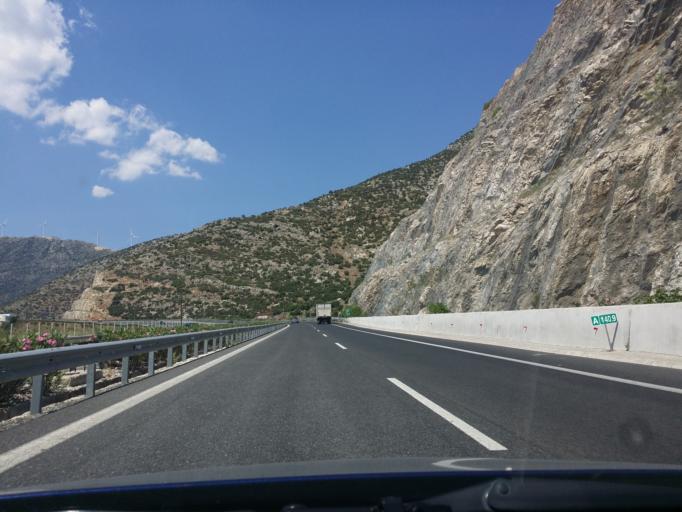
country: GR
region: Peloponnese
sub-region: Nomos Arkadias
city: Tripoli
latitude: 37.6446
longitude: 22.4647
